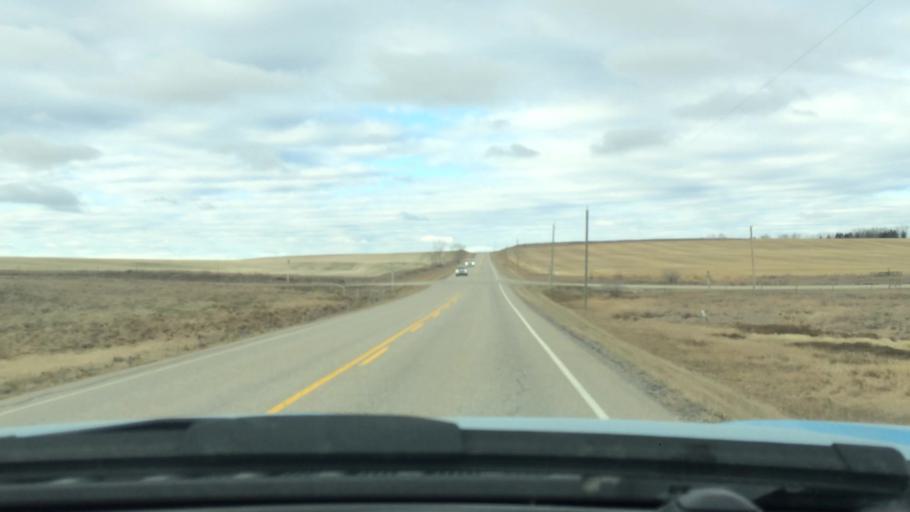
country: CA
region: Alberta
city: Airdrie
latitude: 51.2124
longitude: -114.1161
